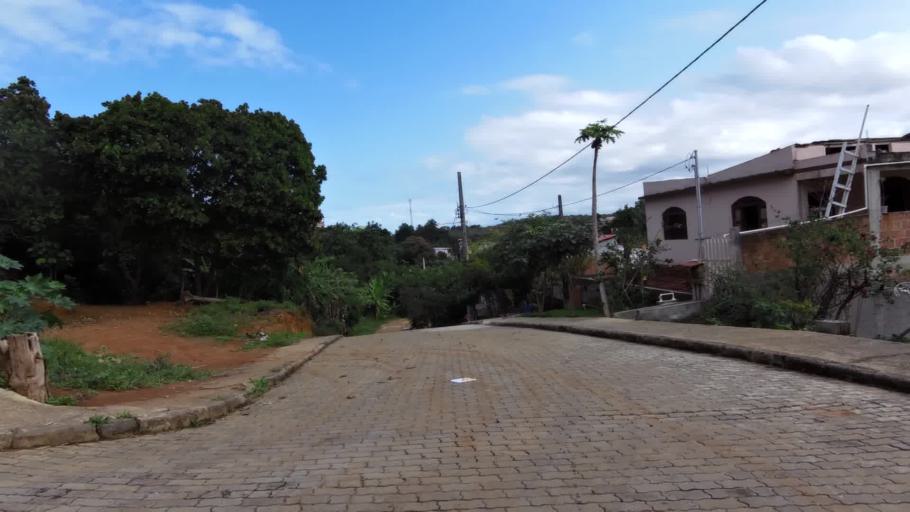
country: BR
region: Espirito Santo
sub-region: Piuma
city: Piuma
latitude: -20.8295
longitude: -40.6994
